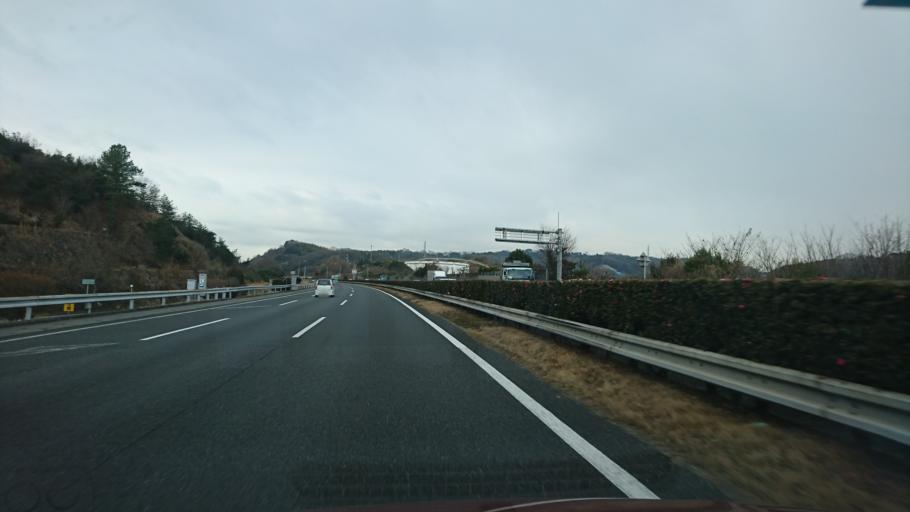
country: JP
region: Okayama
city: Kurashiki
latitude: 34.6261
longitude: 133.7713
